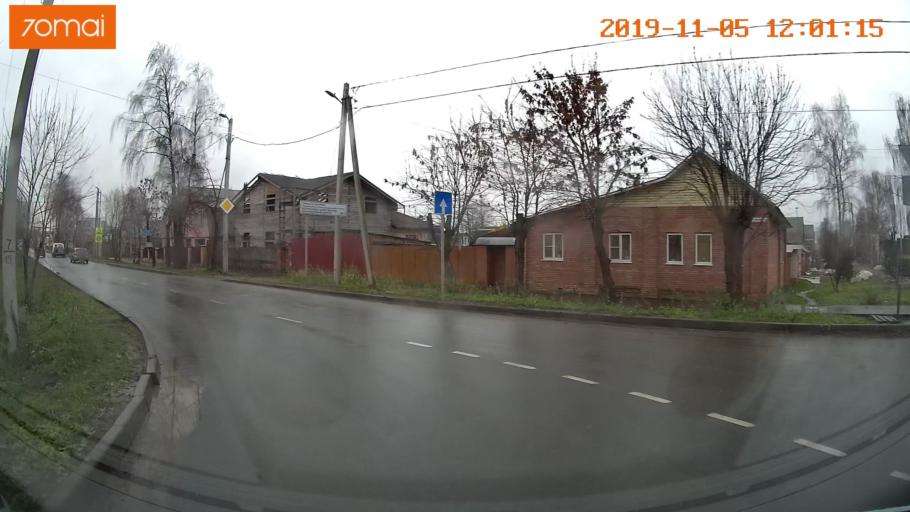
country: RU
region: Ivanovo
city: Kokhma
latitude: 56.9733
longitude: 41.0454
